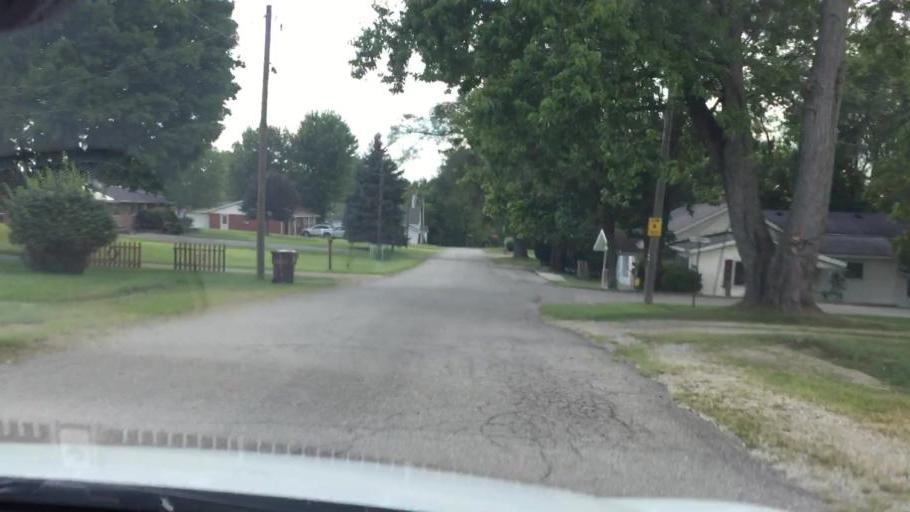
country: US
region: Ohio
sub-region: Champaign County
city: Mechanicsburg
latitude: 40.0740
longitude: -83.5646
